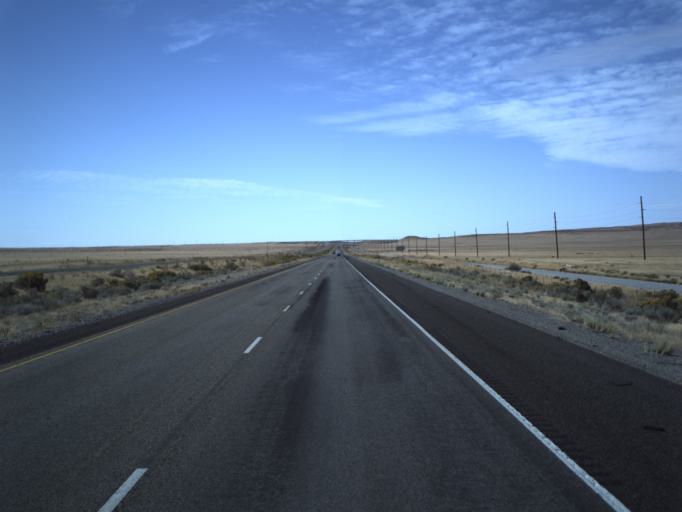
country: US
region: Utah
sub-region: Tooele County
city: Grantsville
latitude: 40.7927
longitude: -112.9529
